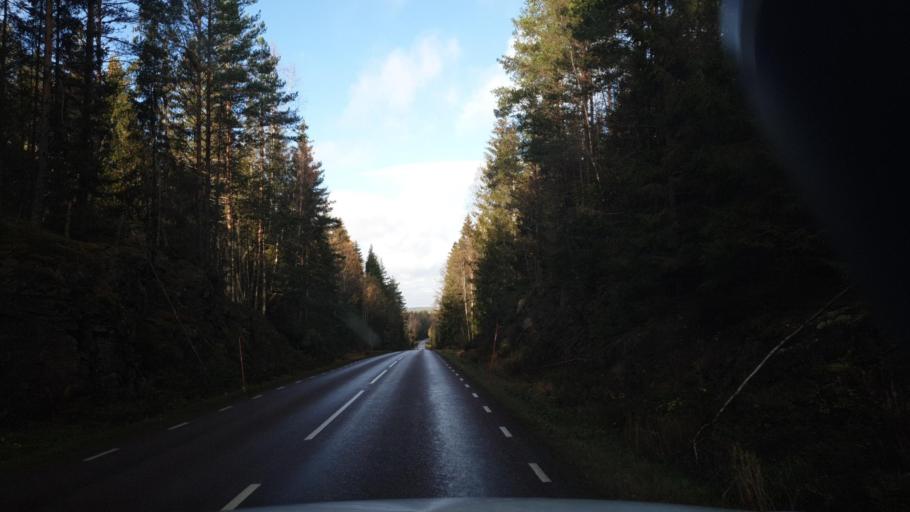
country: SE
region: Vaermland
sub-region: Grums Kommun
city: Grums
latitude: 59.4009
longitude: 13.0174
